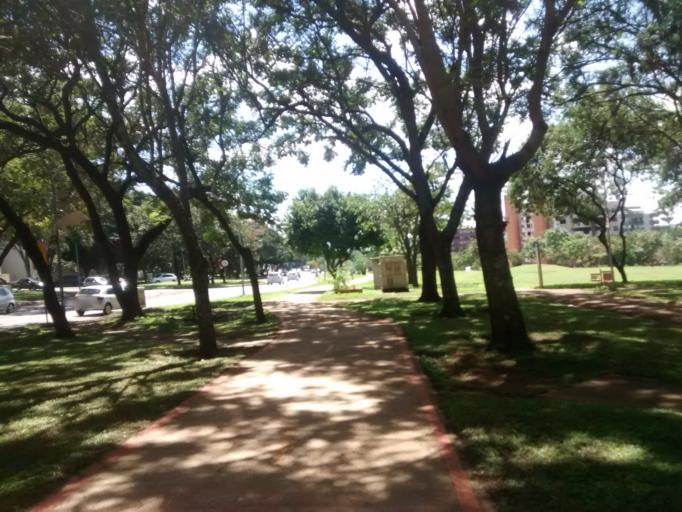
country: BR
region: Federal District
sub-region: Brasilia
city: Brasilia
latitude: -15.7691
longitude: -47.8855
